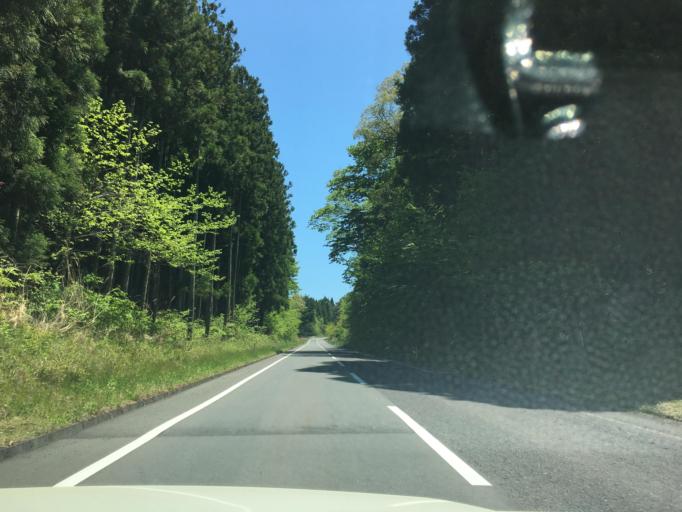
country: JP
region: Fukushima
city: Funehikimachi-funehiki
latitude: 37.3682
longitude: 140.6319
